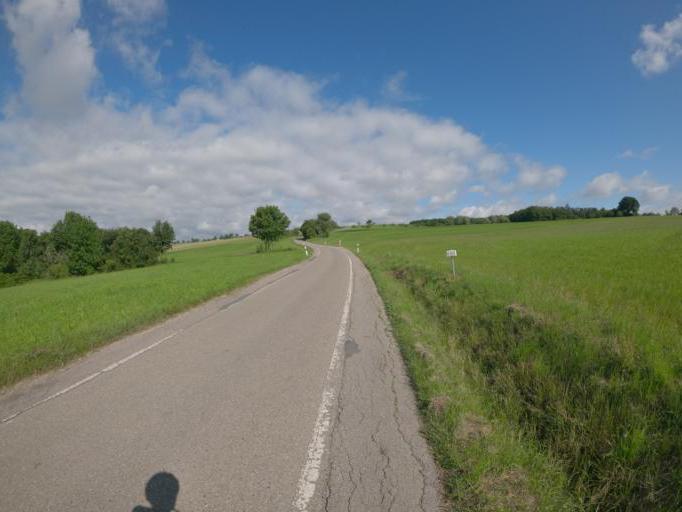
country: DE
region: Baden-Wuerttemberg
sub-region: Regierungsbezirk Stuttgart
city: Ebersbach an der Fils
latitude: 48.7277
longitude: 9.5423
